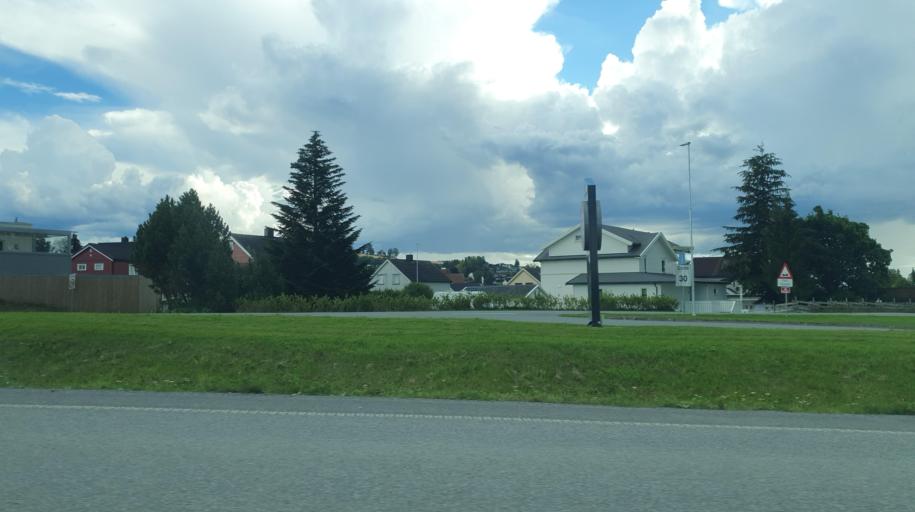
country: NO
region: Nord-Trondelag
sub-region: Levanger
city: Levanger
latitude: 63.7507
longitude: 11.3186
